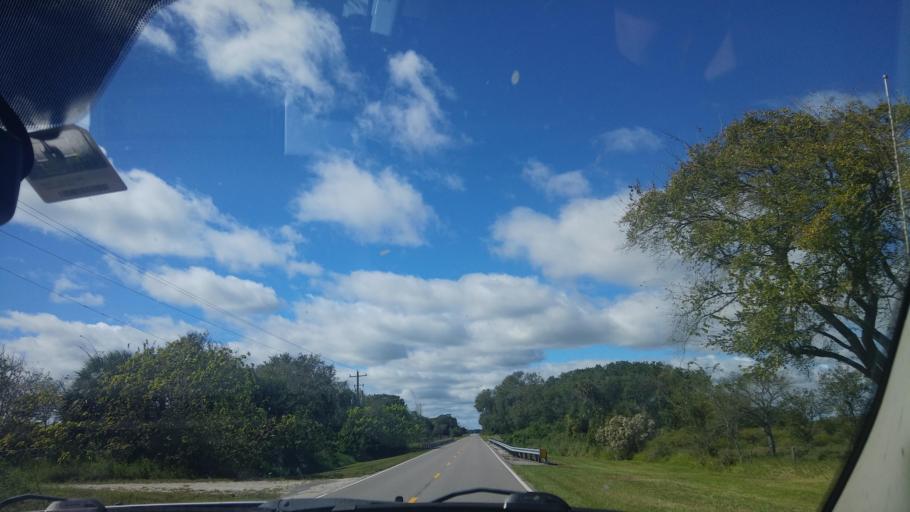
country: US
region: Florida
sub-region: Okeechobee County
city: Cypress Quarters
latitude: 27.3904
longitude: -80.8290
